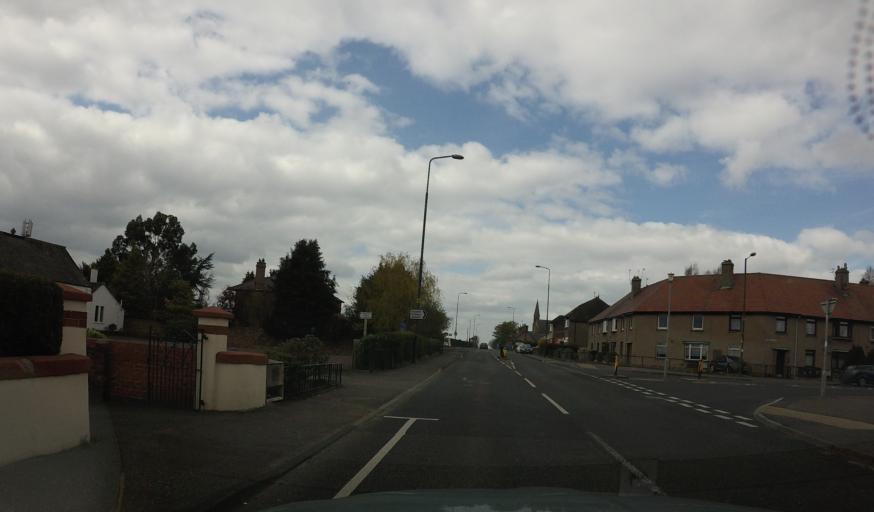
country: GB
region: Scotland
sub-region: Midlothian
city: Gorebridge
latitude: 55.8439
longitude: -3.0493
